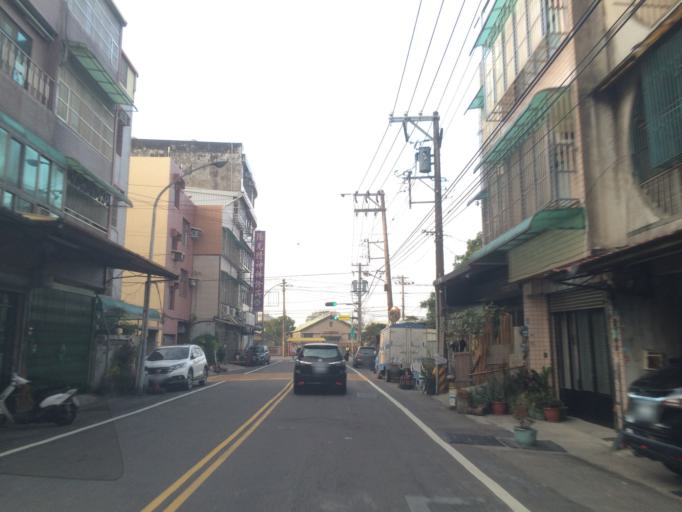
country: TW
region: Taiwan
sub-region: Hsinchu
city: Zhubei
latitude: 24.7222
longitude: 121.0980
